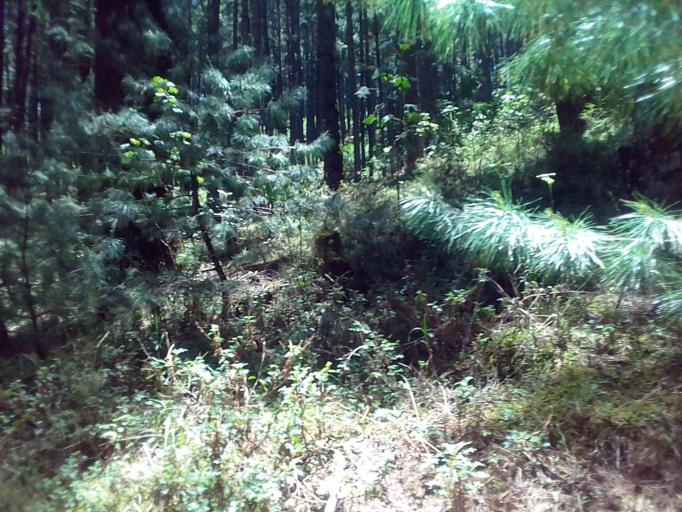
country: MX
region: Mexico City
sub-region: Cuajimalpa de Morelos
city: San Lorenzo Acopilco
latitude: 19.2900
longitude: -99.3348
